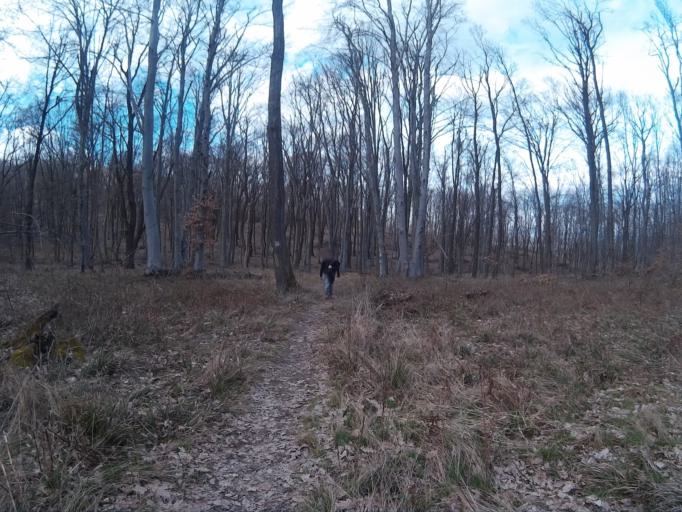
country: HU
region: Pest
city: Kosd
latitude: 47.8354
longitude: 19.1432
